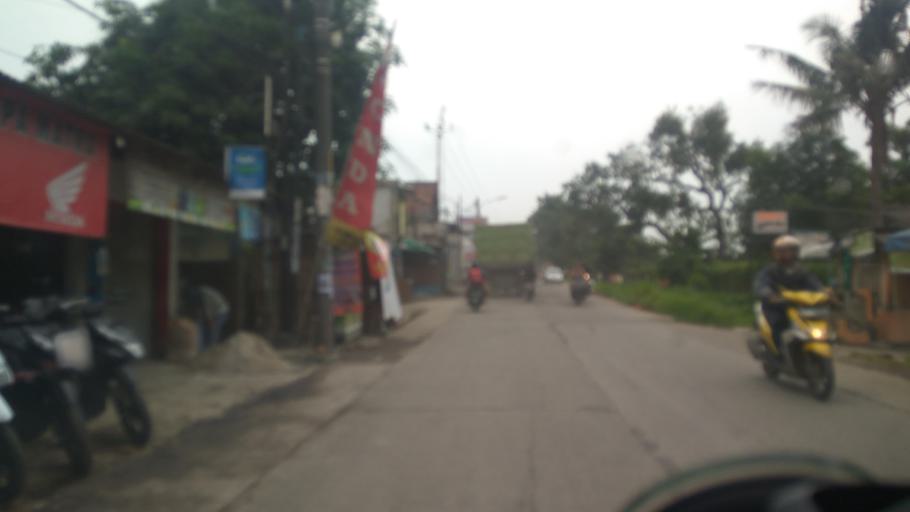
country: ID
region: West Java
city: Bekasi
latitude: -6.1934
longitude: 107.0380
